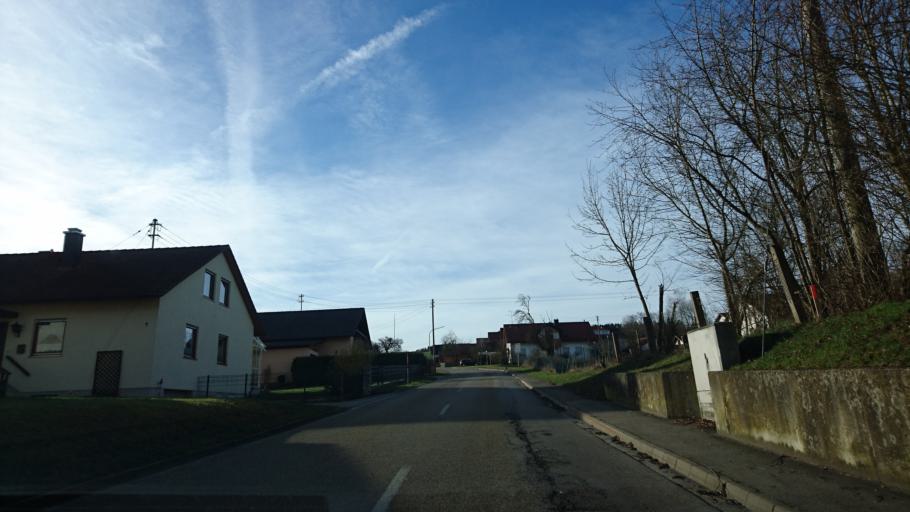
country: DE
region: Bavaria
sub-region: Swabia
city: Altenmunster
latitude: 48.4617
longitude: 10.6023
